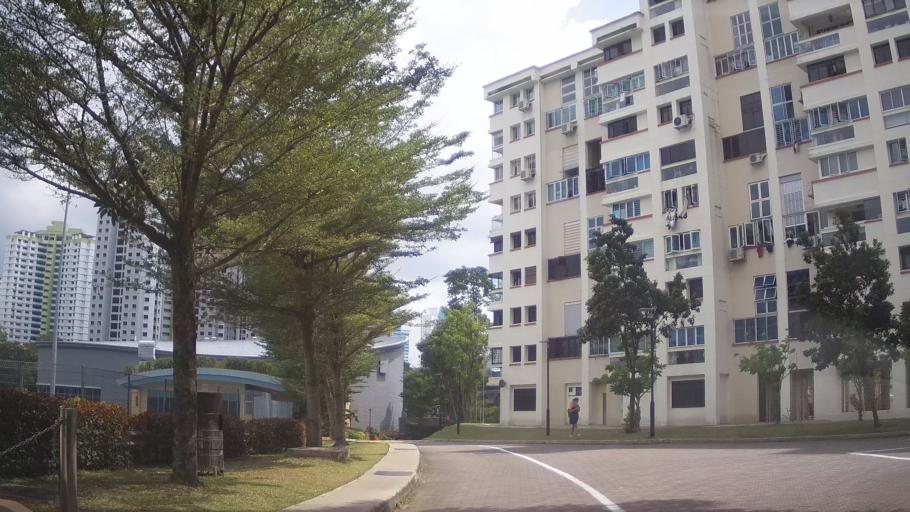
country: MY
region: Johor
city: Johor Bahru
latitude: 1.3829
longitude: 103.7644
